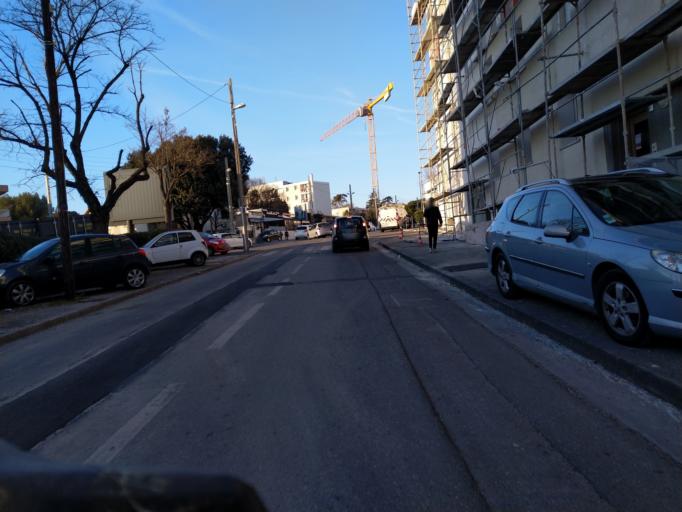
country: FR
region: Provence-Alpes-Cote d'Azur
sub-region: Departement des Bouches-du-Rhone
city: Marseille 12
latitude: 43.2983
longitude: 5.4369
